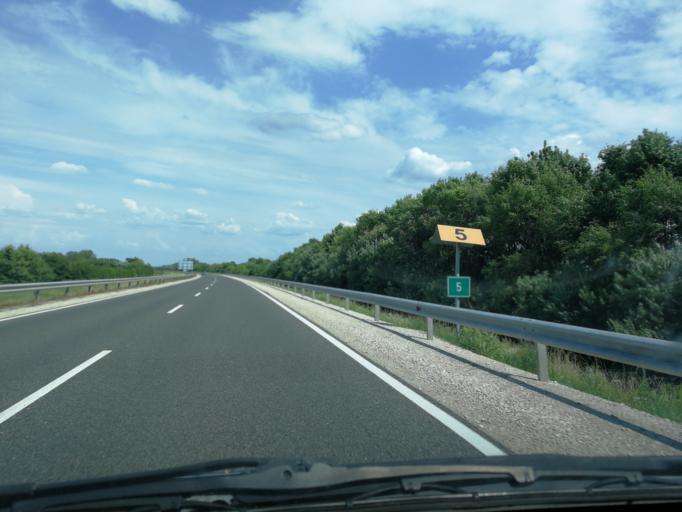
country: HU
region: Tolna
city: Tolna
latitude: 46.3767
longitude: 18.7734
